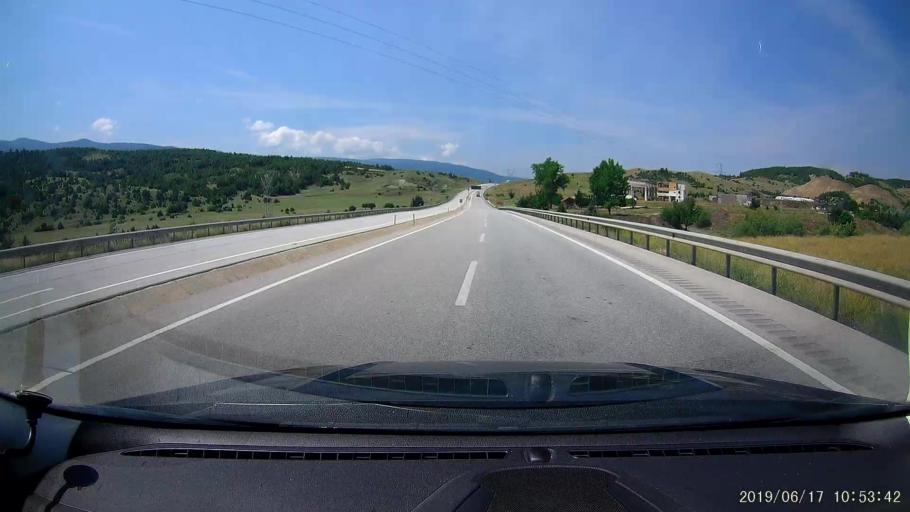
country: TR
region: Corum
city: Hacihamza
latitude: 41.0805
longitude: 34.3156
